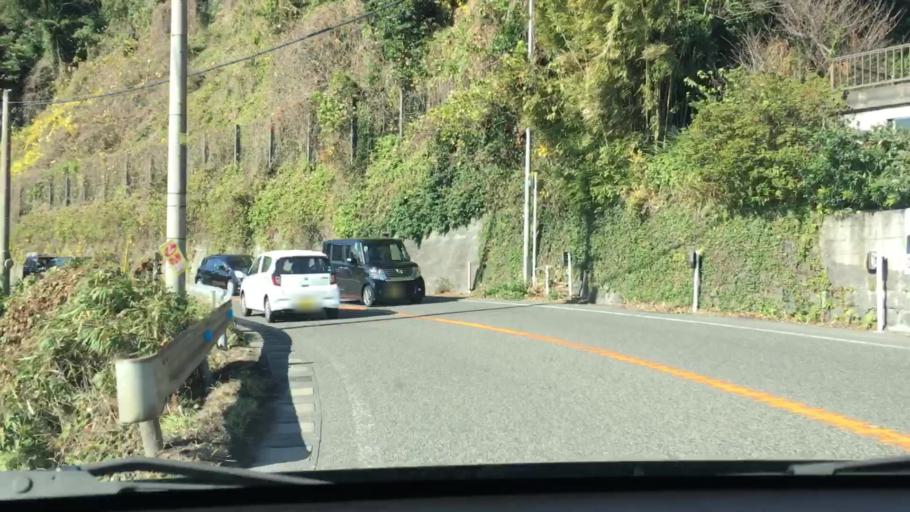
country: JP
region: Kagoshima
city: Kagoshima-shi
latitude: 31.6237
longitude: 130.5884
